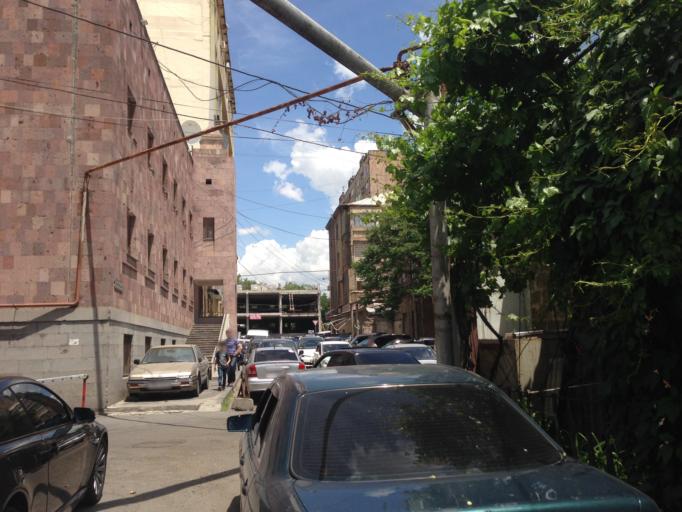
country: AM
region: Yerevan
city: Yerevan
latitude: 40.1729
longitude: 44.5099
